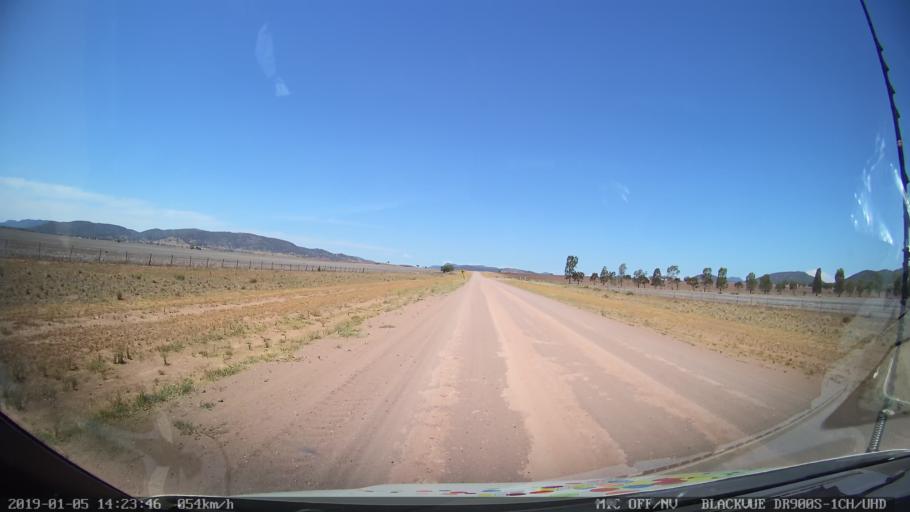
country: AU
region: New South Wales
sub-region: Liverpool Plains
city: Quirindi
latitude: -31.2421
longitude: 150.5334
